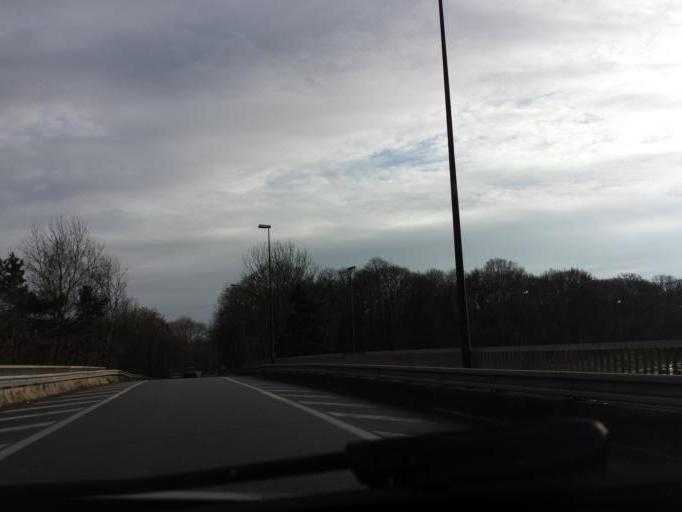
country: FR
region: Ile-de-France
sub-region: Departement des Hauts-de-Seine
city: Chatenay-Malabry
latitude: 48.7724
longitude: 2.2427
